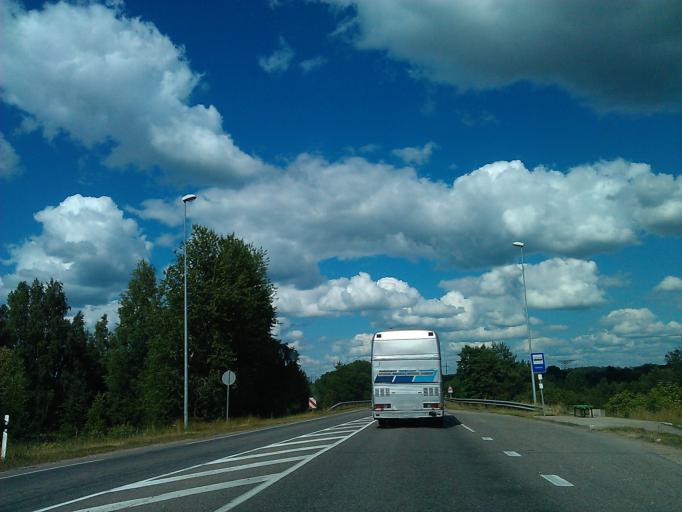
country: LV
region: Rezekne
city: Rezekne
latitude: 56.5407
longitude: 27.3006
